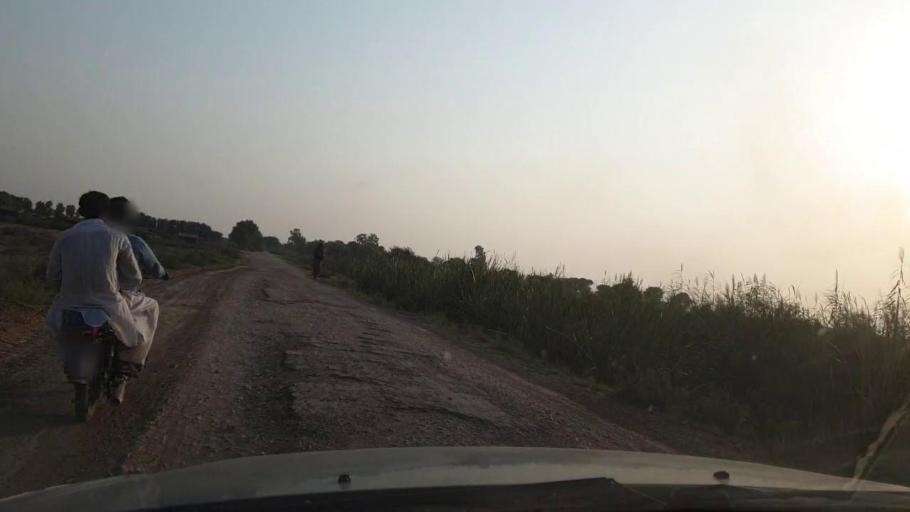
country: PK
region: Sindh
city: Tando Muhammad Khan
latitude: 25.0199
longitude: 68.4392
